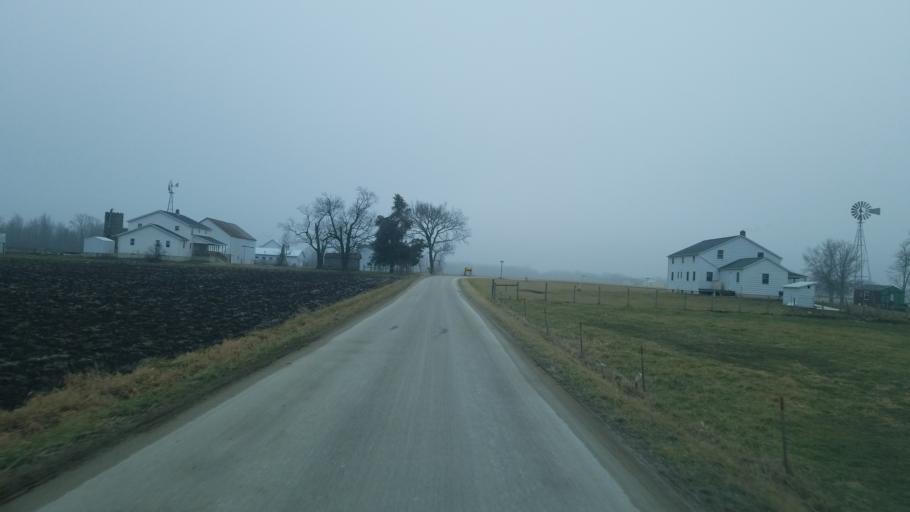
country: US
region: Indiana
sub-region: Adams County
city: Geneva
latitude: 40.5976
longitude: -84.9306
